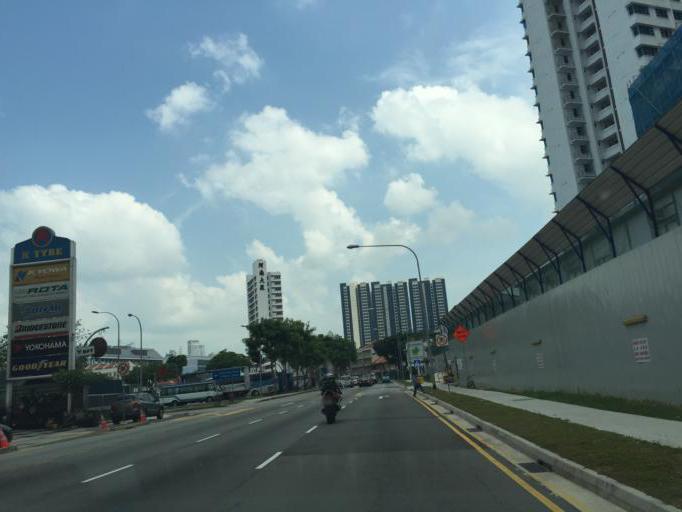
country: SG
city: Singapore
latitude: 1.3152
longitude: 103.8613
